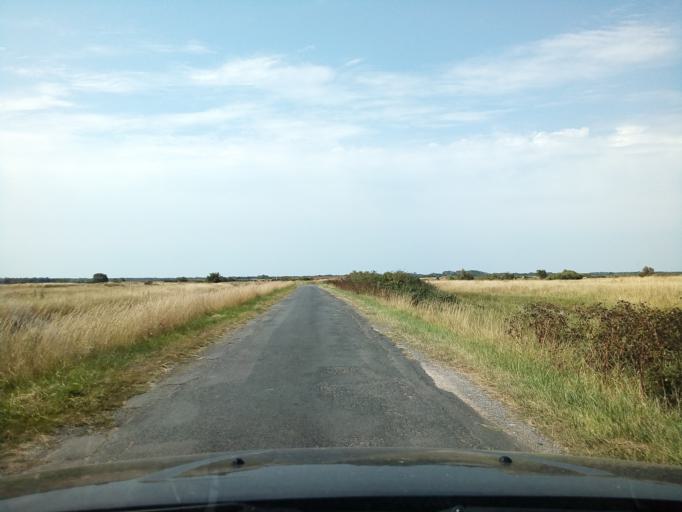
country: FR
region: Poitou-Charentes
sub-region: Departement de la Charente-Maritime
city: Boyard-Ville
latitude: 45.9535
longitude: -1.2633
